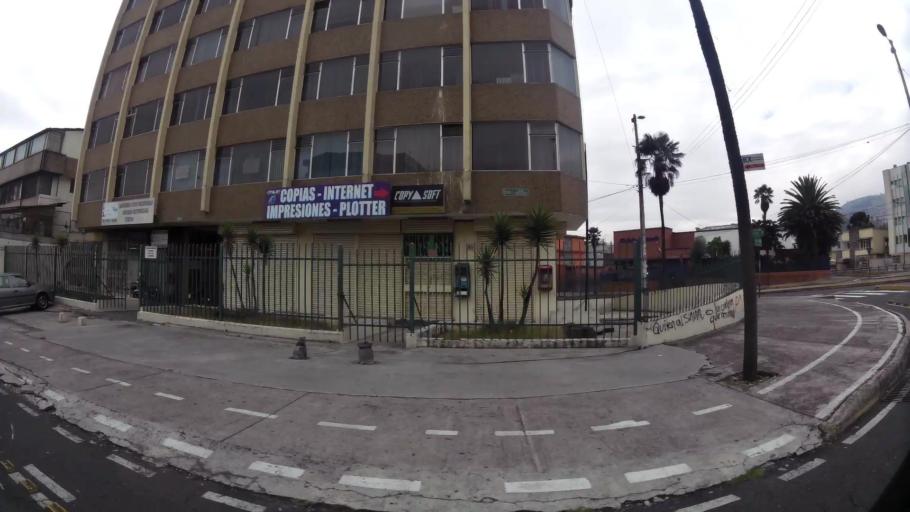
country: EC
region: Pichincha
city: Quito
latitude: -0.2022
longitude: -78.5011
